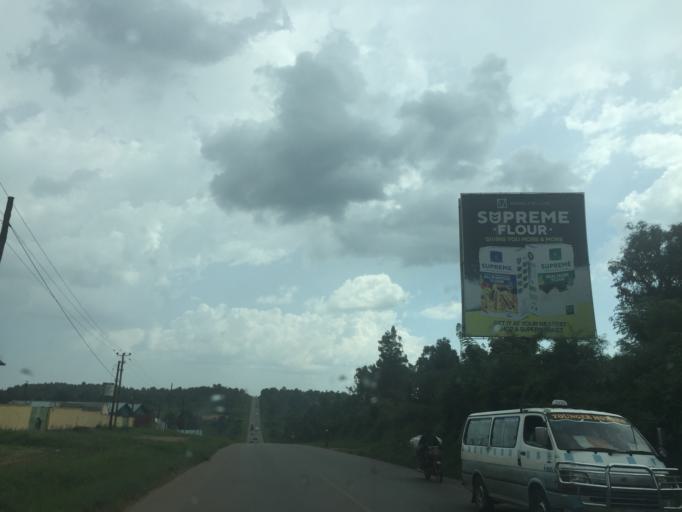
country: UG
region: Central Region
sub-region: Luwero District
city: Wobulenzi
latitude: 0.6057
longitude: 32.5322
